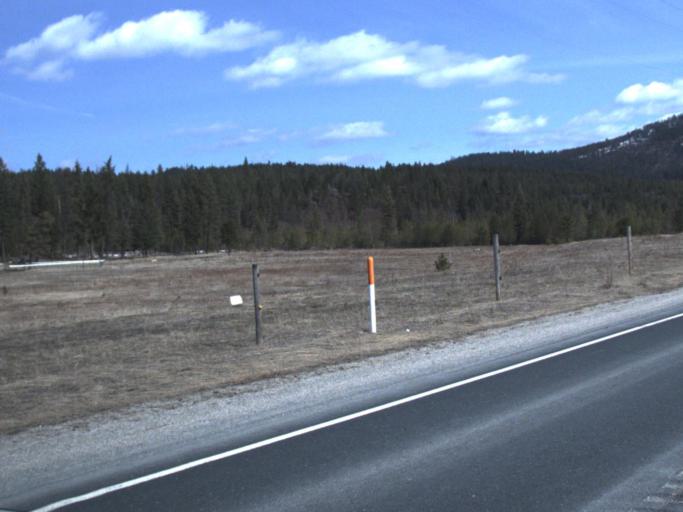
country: US
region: Washington
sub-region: Stevens County
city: Chewelah
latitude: 48.5188
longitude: -117.6487
